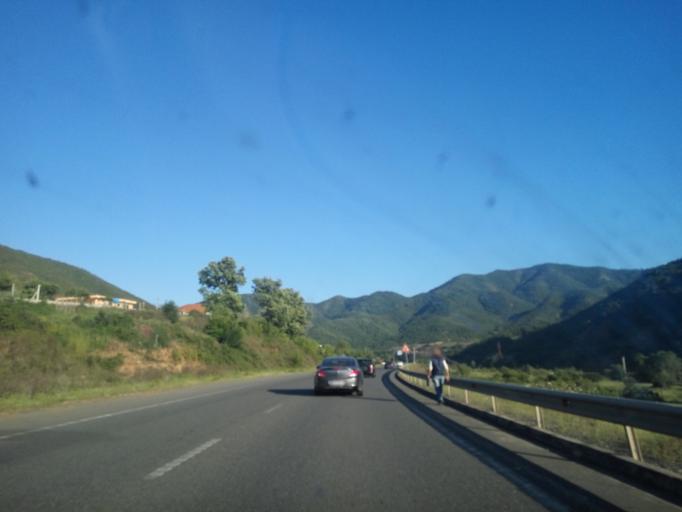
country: AL
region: Lezhe
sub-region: Rrethi i Mirdites
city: Rubik
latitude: 41.7897
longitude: 19.8170
